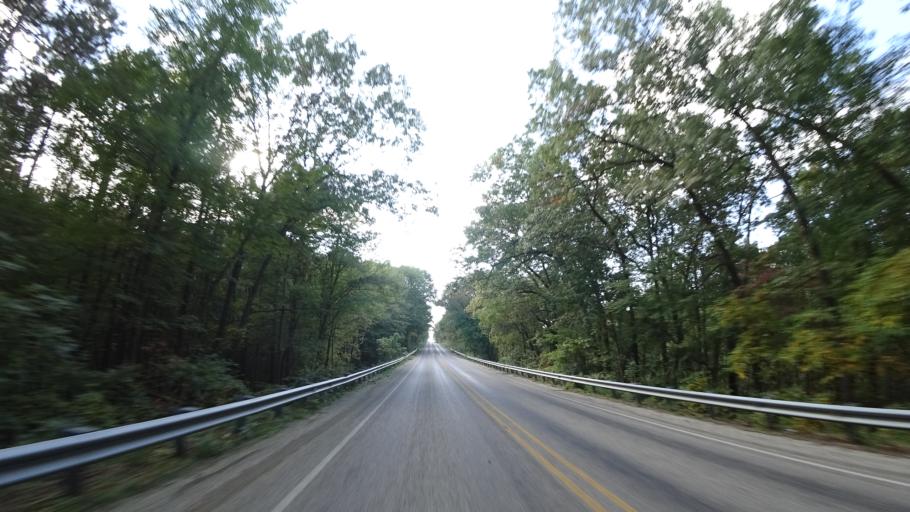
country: US
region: Michigan
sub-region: Saint Joseph County
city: Sturgis
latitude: 41.8539
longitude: -85.4497
